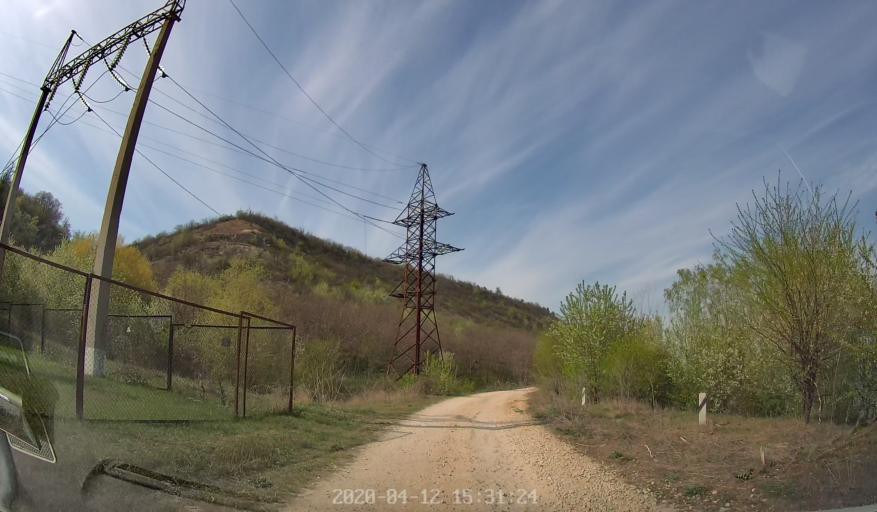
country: MD
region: Telenesti
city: Cocieri
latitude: 47.3235
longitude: 29.0742
